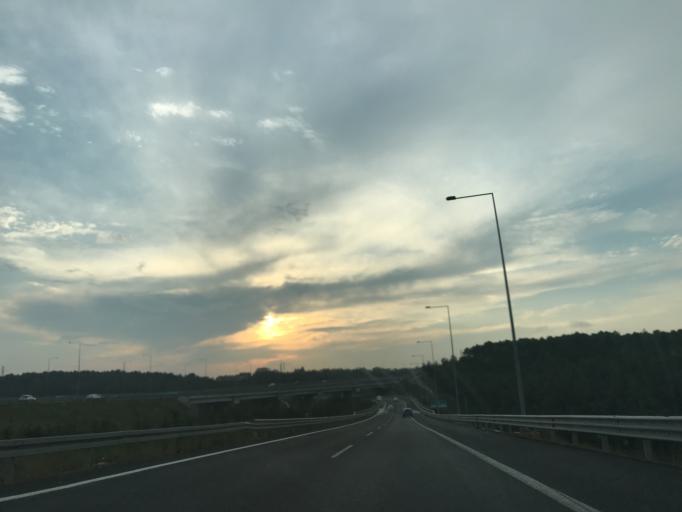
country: TR
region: Istanbul
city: Umraniye
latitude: 41.0497
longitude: 29.1303
